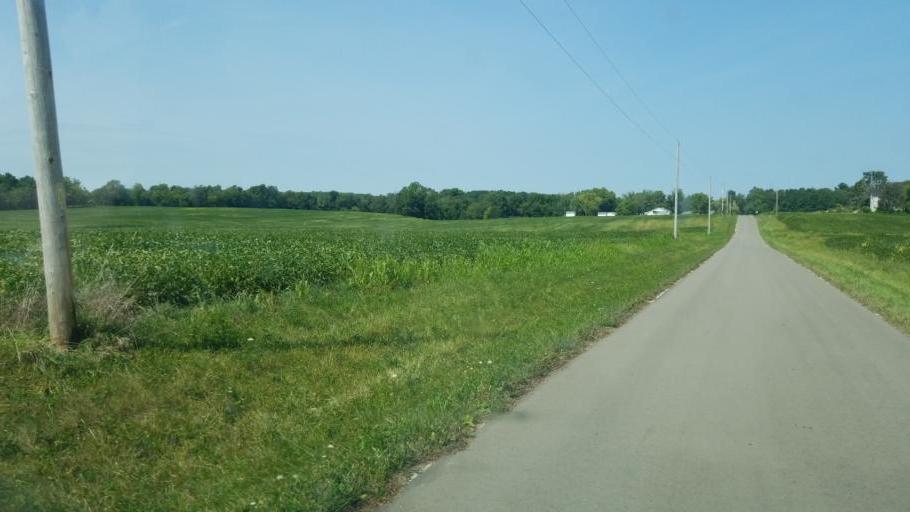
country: US
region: Ohio
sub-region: Crawford County
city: Bucyrus
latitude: 40.9219
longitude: -83.0742
